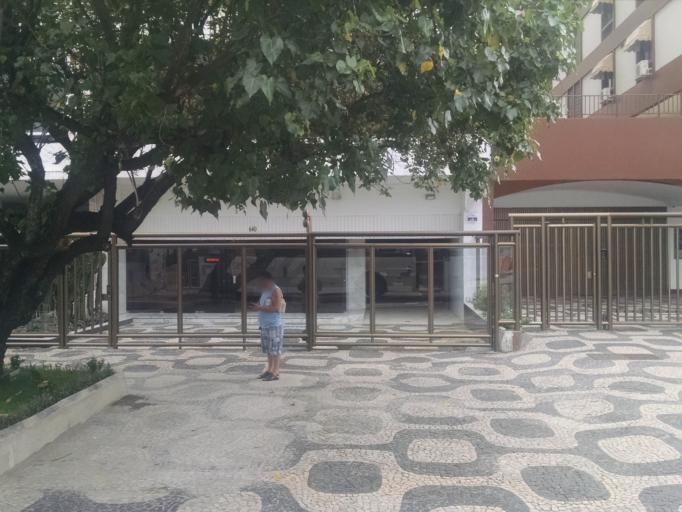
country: BR
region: Rio de Janeiro
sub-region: Rio De Janeiro
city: Rio de Janeiro
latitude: -22.9853
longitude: -43.1925
